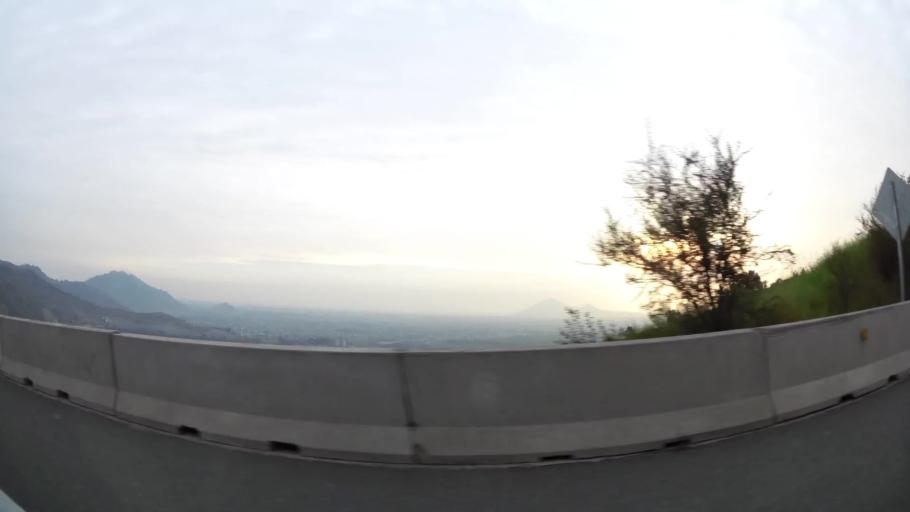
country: CL
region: Santiago Metropolitan
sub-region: Provincia de Santiago
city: Villa Presidente Frei, Nunoa, Santiago, Chile
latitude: -33.3833
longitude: -70.6047
